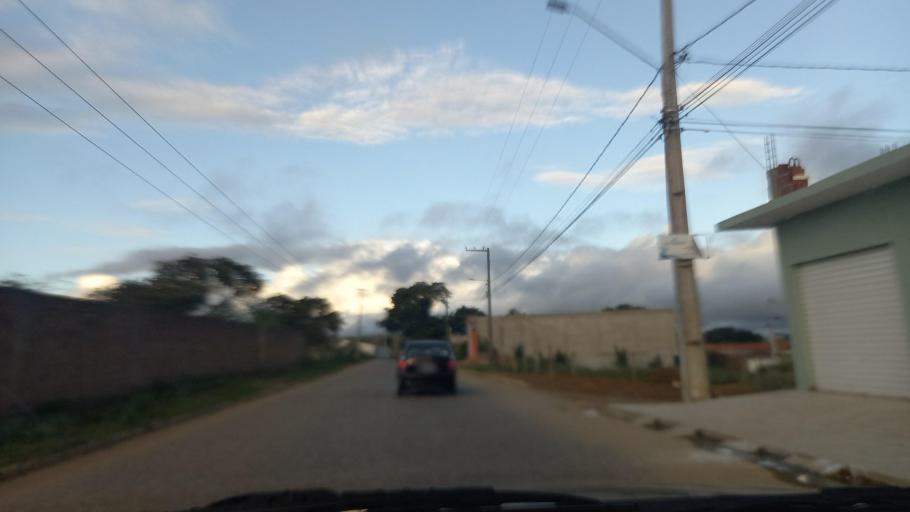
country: BR
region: Pernambuco
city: Garanhuns
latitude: -8.8907
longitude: -36.4507
